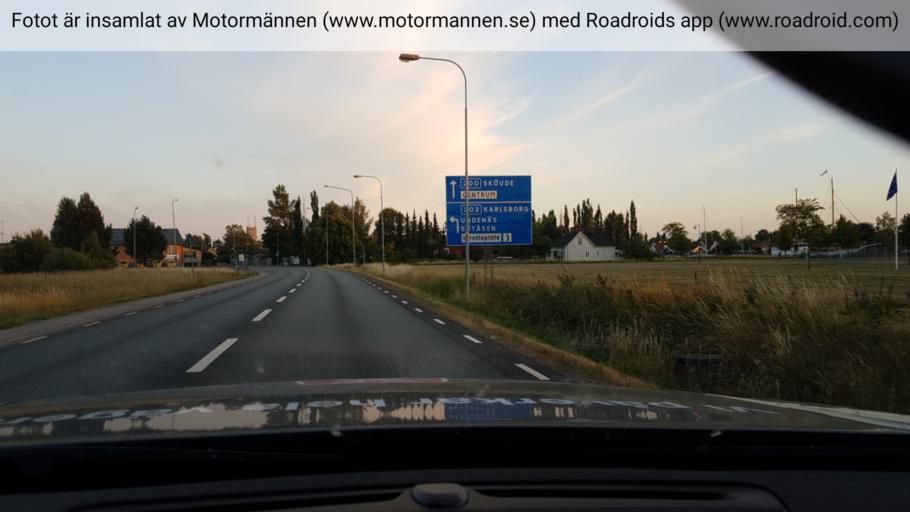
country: SE
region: Vaestra Goetaland
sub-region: Toreboda Kommun
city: Toereboda
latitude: 58.7138
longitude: 14.1315
